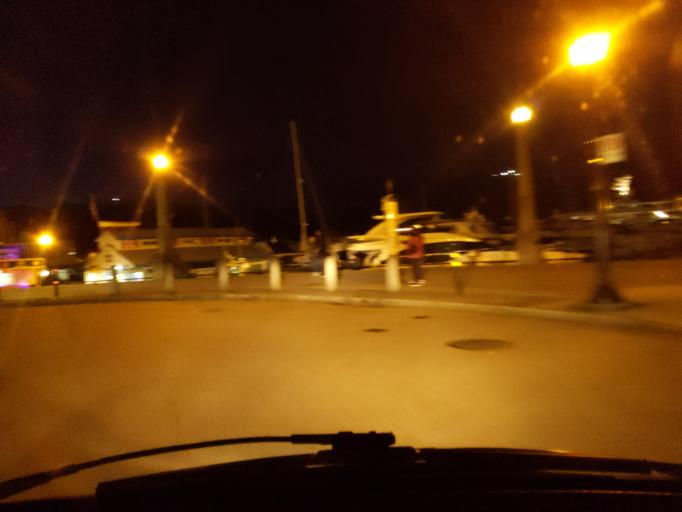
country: CA
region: British Columbia
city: West End
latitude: 49.2904
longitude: -123.1261
